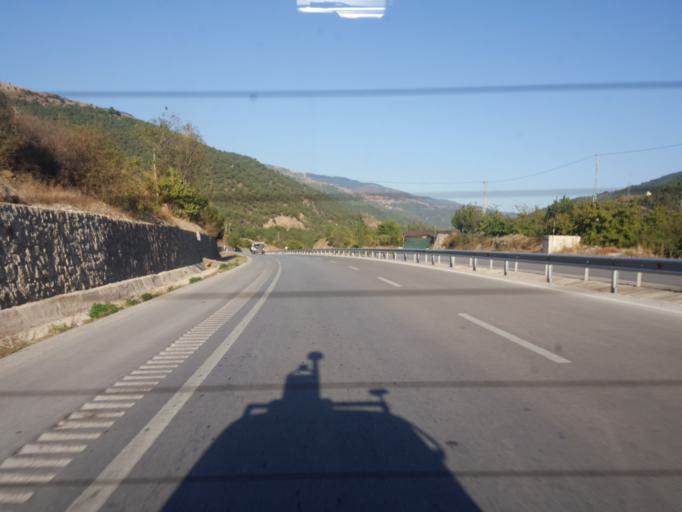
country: TR
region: Amasya
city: Akdag
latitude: 40.7448
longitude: 36.0153
